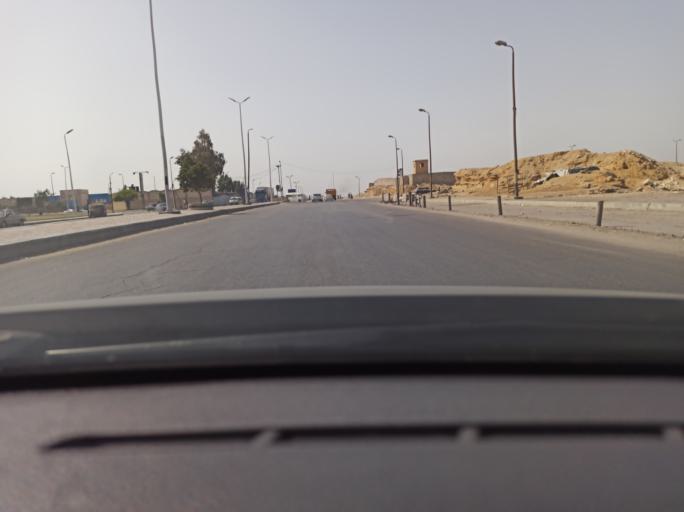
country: EG
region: Muhafazat al Qahirah
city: Halwan
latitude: 29.8209
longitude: 31.3527
